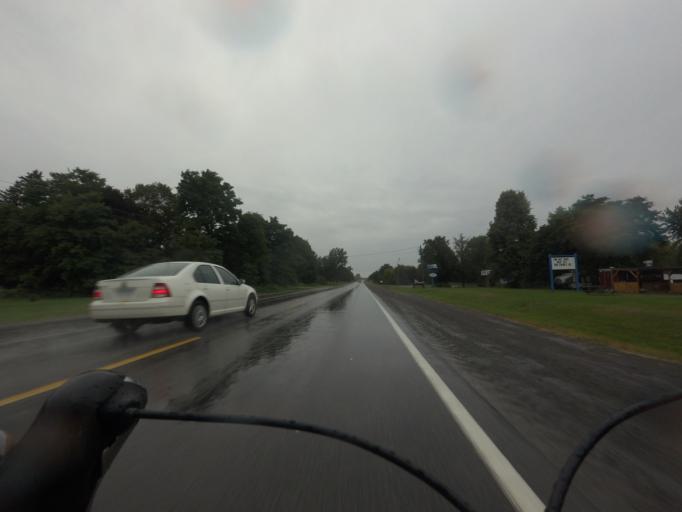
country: CA
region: Ontario
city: Bells Corners
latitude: 45.1824
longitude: -75.7209
